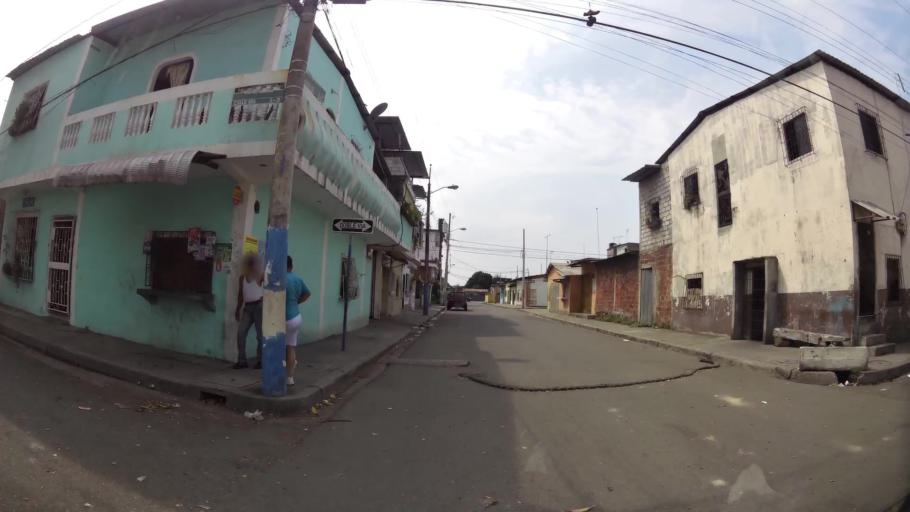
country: EC
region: Guayas
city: Guayaquil
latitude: -2.2401
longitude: -79.9090
